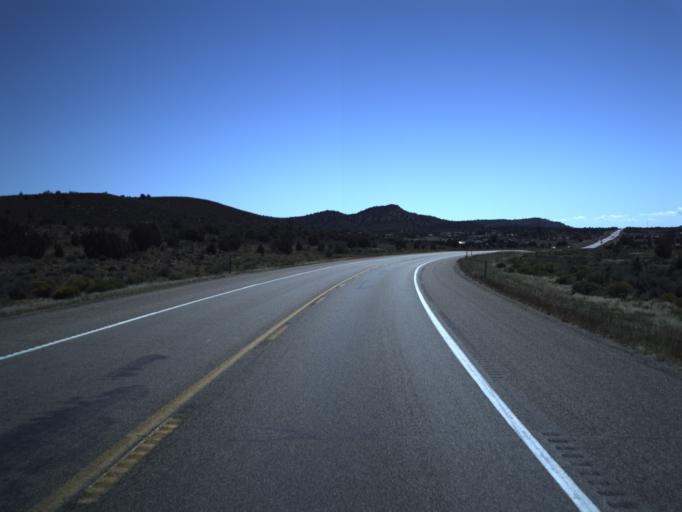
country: US
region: Utah
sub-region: Washington County
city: Ivins
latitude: 37.3176
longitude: -113.6798
